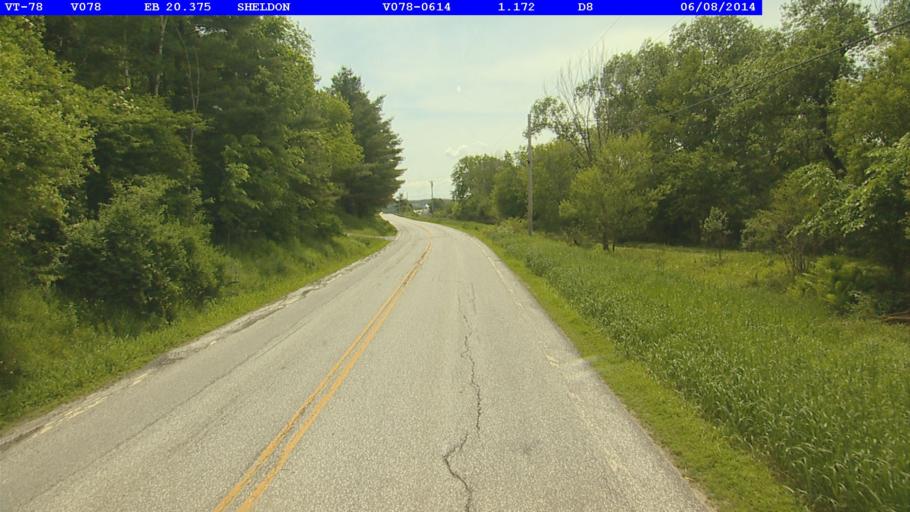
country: US
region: Vermont
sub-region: Franklin County
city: Enosburg Falls
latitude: 44.9108
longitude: -72.9548
